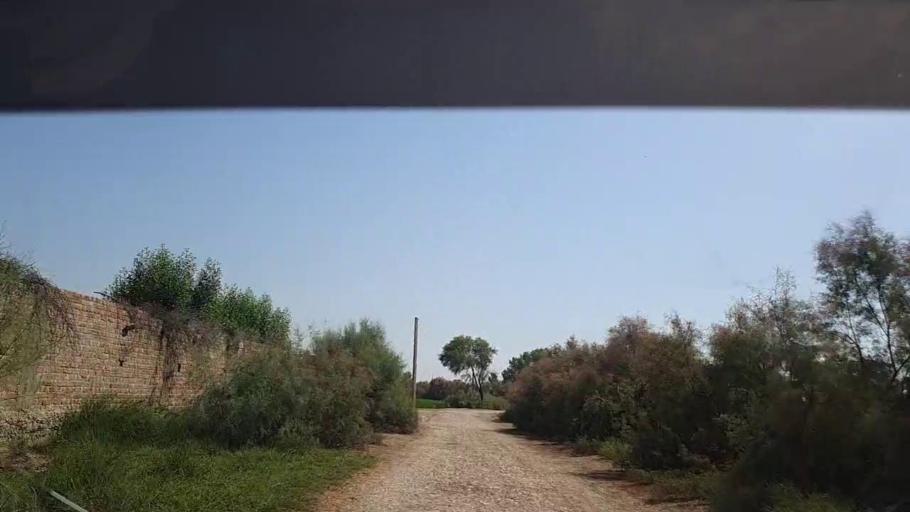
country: PK
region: Sindh
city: Ghauspur
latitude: 28.2087
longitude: 69.0780
